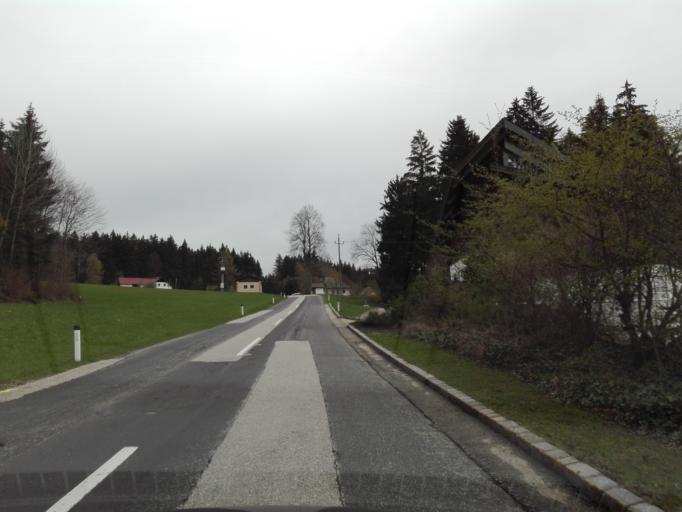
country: AT
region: Upper Austria
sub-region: Politischer Bezirk Rohrbach
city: Ulrichsberg
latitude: 48.6943
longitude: 13.9206
